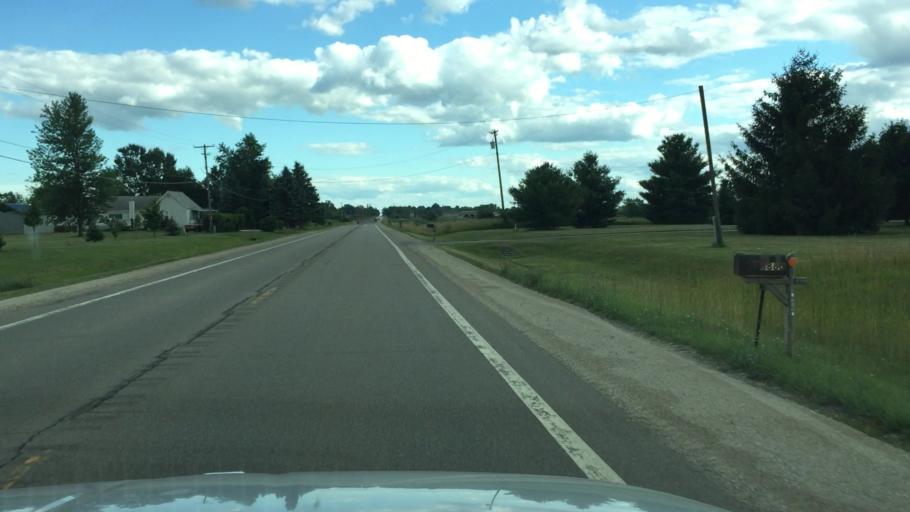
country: US
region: Michigan
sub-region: Saint Clair County
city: Yale
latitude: 43.1550
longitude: -82.8002
